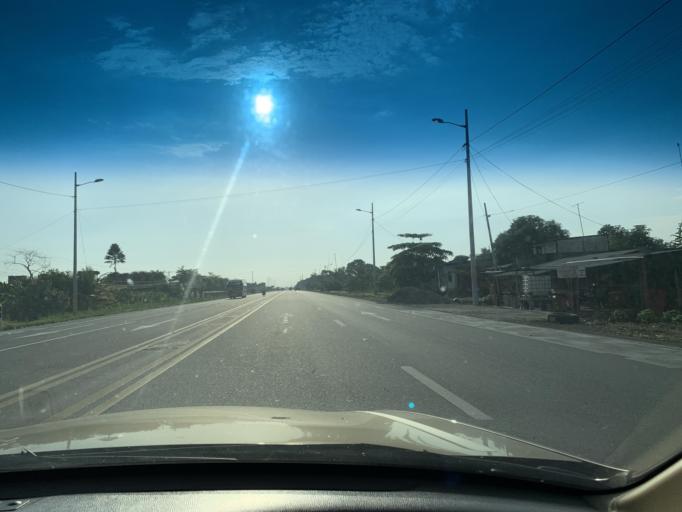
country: EC
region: Guayas
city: Naranjito
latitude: -2.2561
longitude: -79.5969
